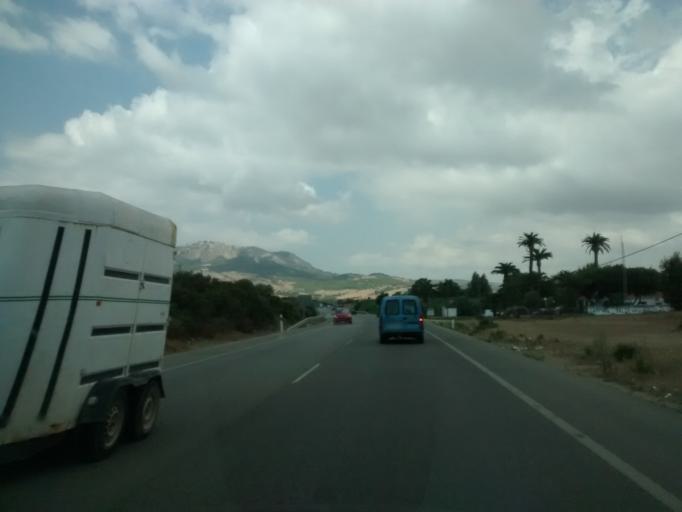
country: ES
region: Andalusia
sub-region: Provincia de Cadiz
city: Tarifa
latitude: 36.0682
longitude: -5.6798
